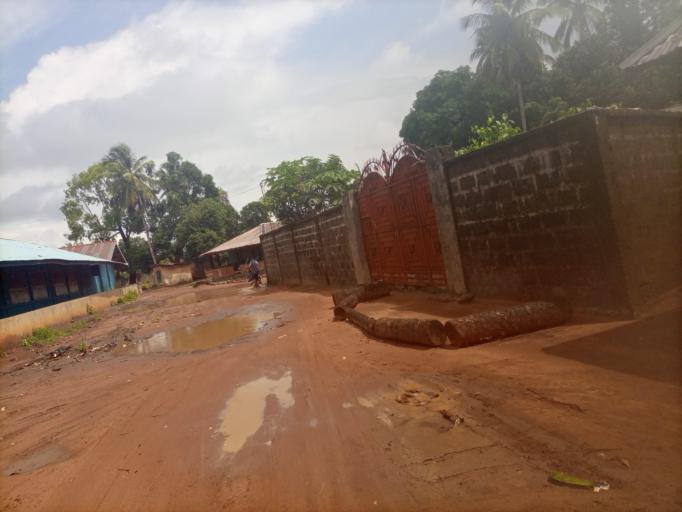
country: SL
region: Northern Province
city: Tintafor
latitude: 8.6290
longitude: -13.2149
